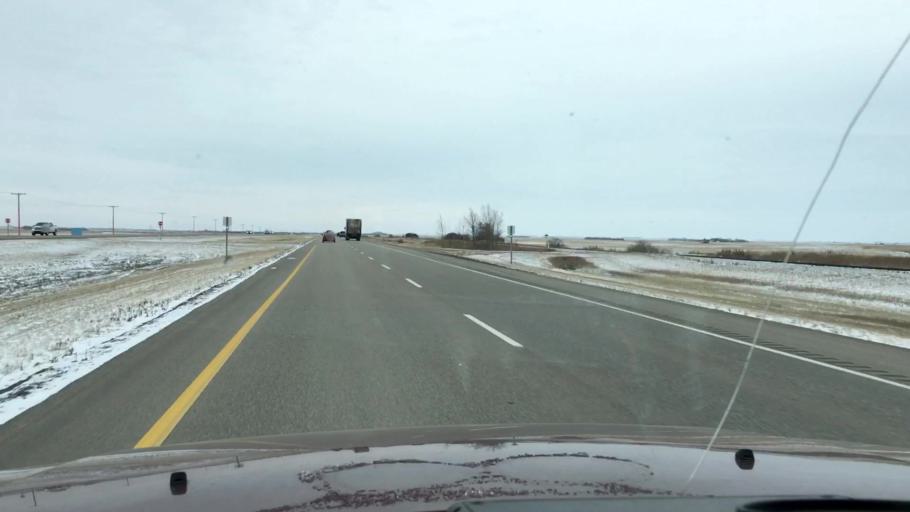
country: CA
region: Saskatchewan
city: Watrous
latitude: 51.1918
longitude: -105.9496
